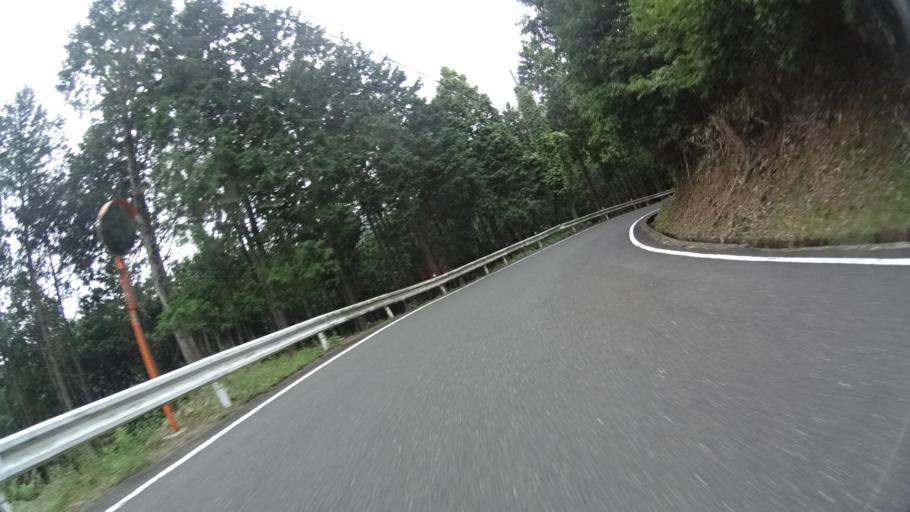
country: JP
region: Kyoto
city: Miyazu
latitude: 35.4704
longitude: 135.1531
